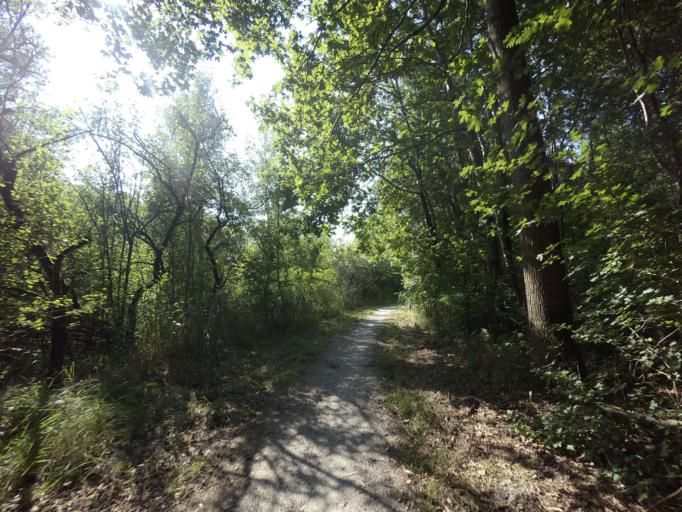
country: NL
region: Groningen
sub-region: Gemeente De Marne
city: Ulrum
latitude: 53.3988
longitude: 6.2609
